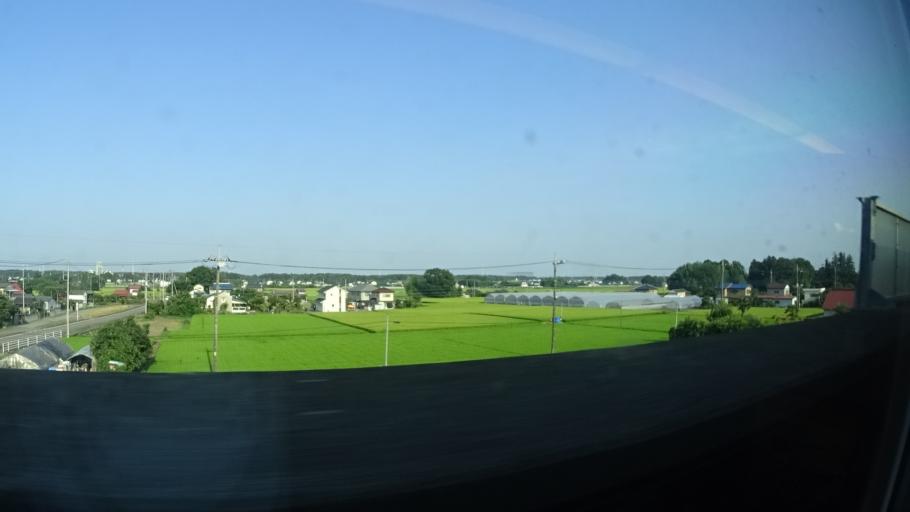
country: JP
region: Tochigi
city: Utsunomiya-shi
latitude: 36.6202
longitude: 139.9082
